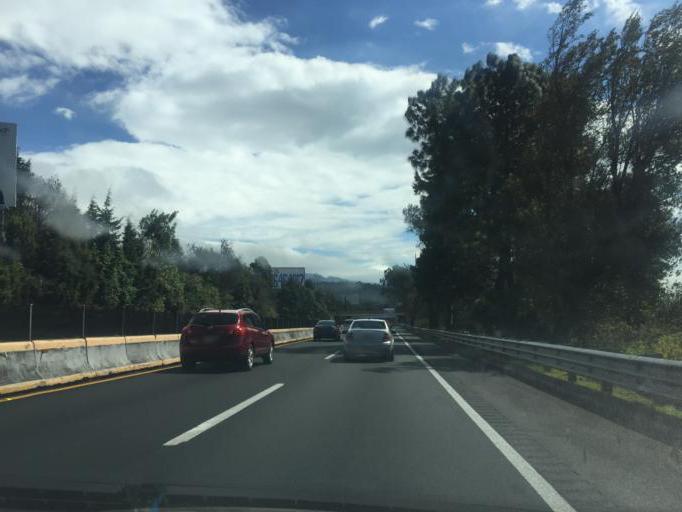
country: MX
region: Morelos
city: Tres Marias
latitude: 19.0319
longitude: -99.2093
